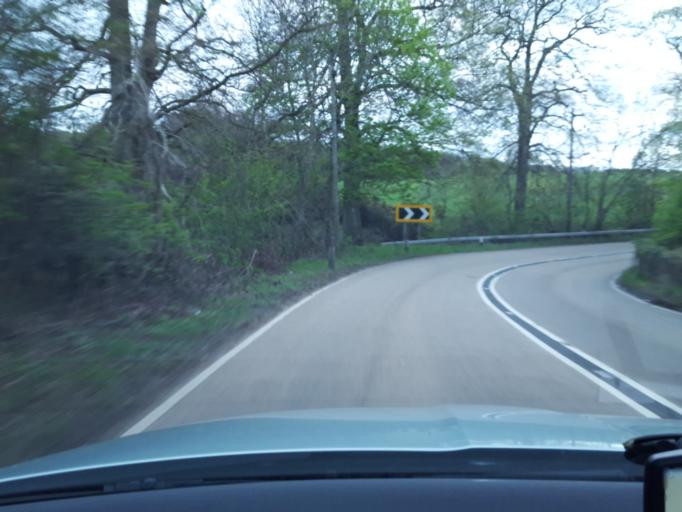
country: GB
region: Scotland
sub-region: West Lothian
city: Linlithgow
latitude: 55.9580
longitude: -3.6499
